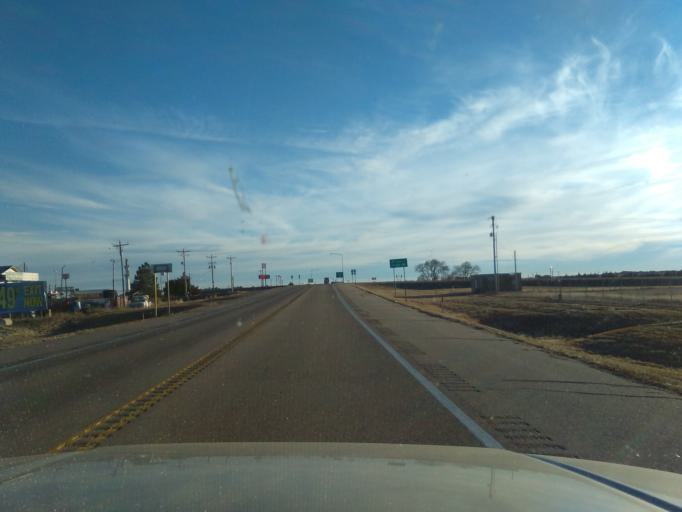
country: US
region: Kansas
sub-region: Logan County
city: Oakley
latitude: 39.1923
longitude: -100.8699
